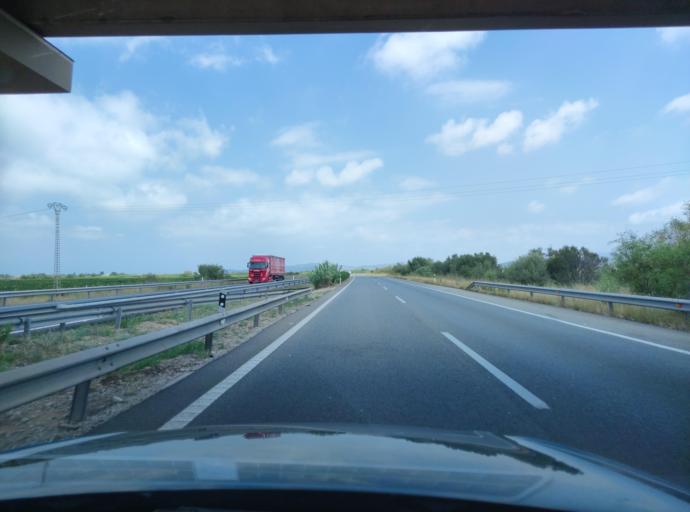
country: ES
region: Catalonia
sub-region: Provincia de Tarragona
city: Alcanar
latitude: 40.5251
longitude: 0.4173
